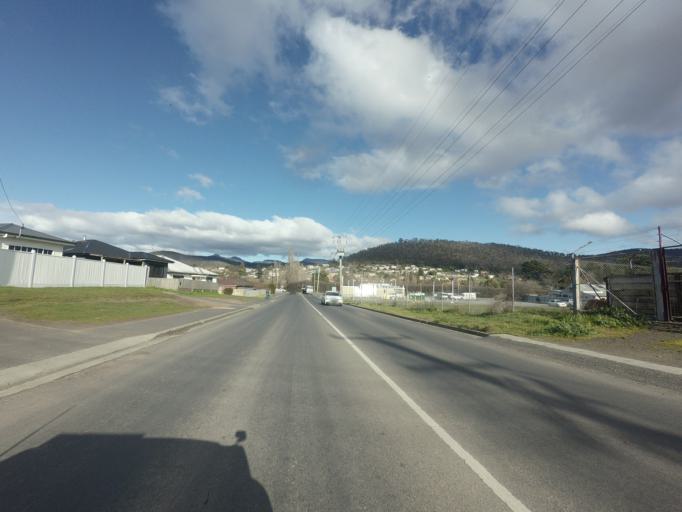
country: AU
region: Tasmania
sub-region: Derwent Valley
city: New Norfolk
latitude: -42.7766
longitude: 147.0536
